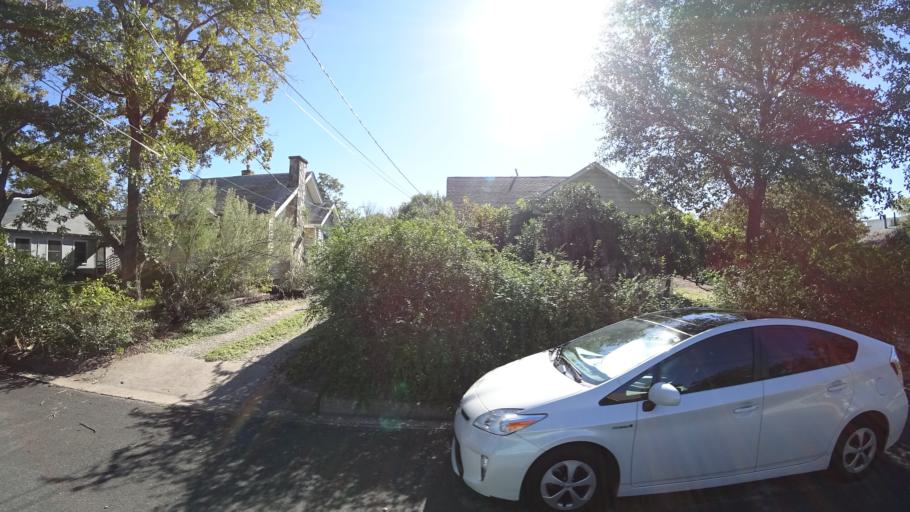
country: US
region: Texas
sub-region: Travis County
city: Austin
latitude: 30.3229
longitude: -97.7378
